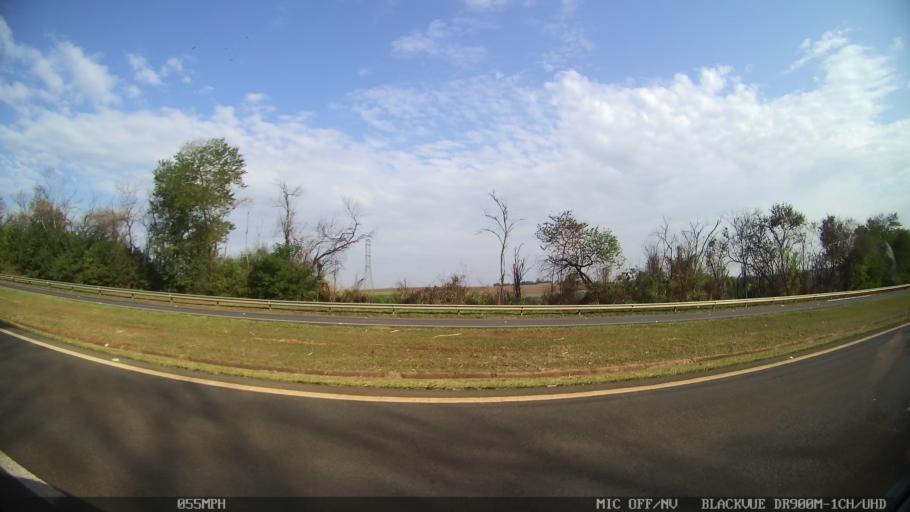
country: BR
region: Sao Paulo
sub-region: Cosmopolis
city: Cosmopolis
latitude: -22.6513
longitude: -47.1965
